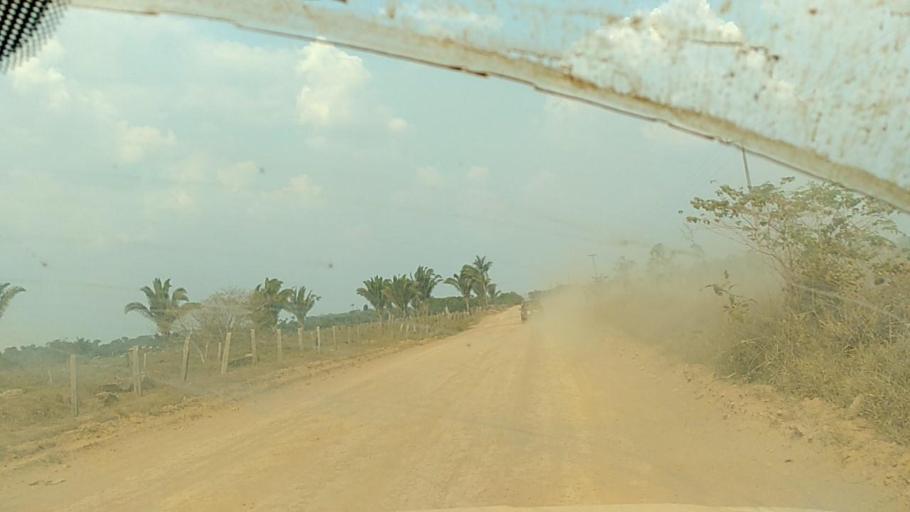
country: BR
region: Rondonia
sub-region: Porto Velho
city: Porto Velho
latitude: -8.6829
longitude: -63.2370
